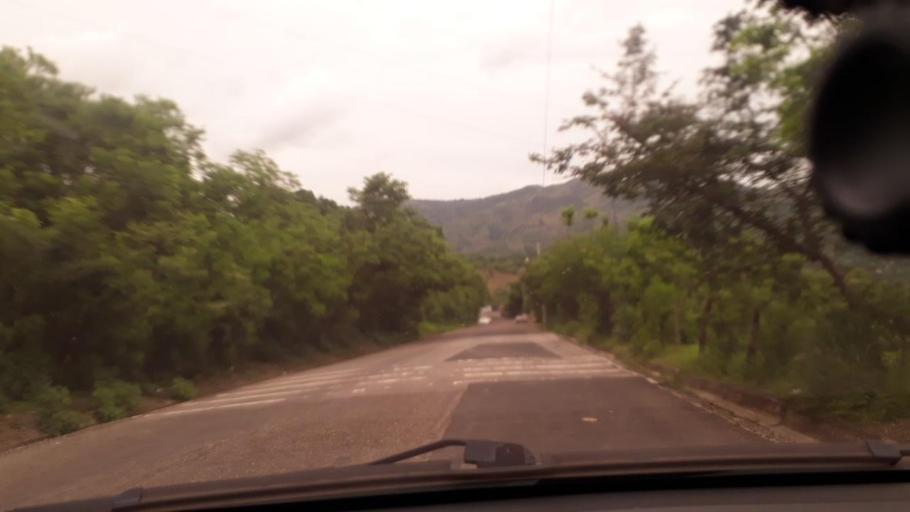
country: GT
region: Chiquimula
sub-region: Municipio de San Juan Ermita
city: San Juan Ermita
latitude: 14.7423
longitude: -89.4670
